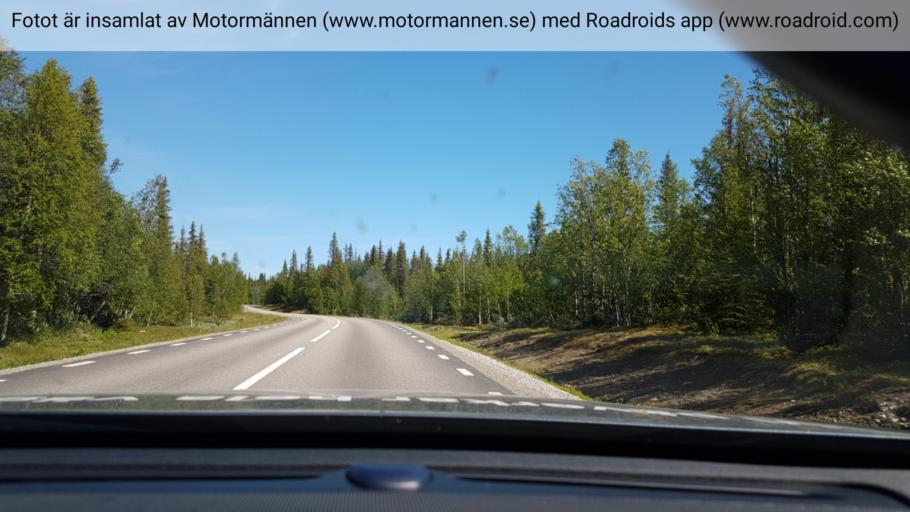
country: SE
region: Vaesterbotten
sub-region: Asele Kommun
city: Insjon
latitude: 64.7323
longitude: 17.4439
